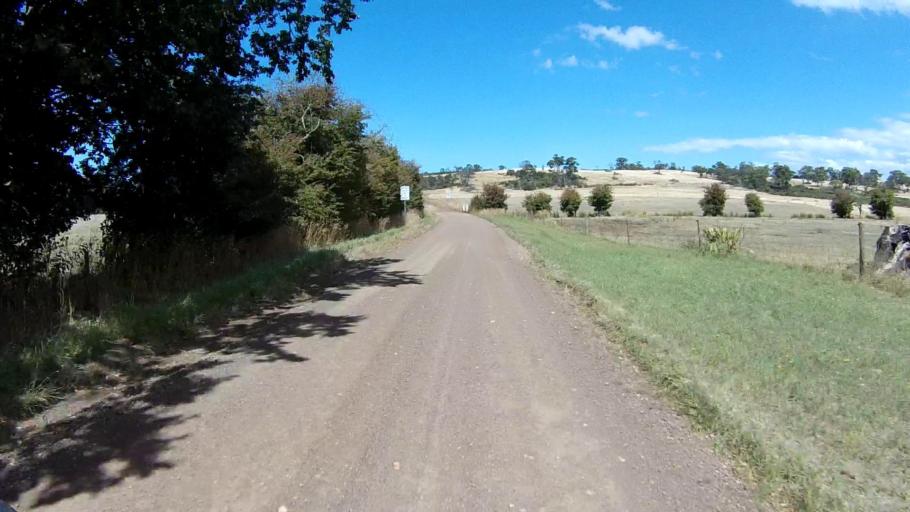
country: AU
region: Tasmania
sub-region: Break O'Day
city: St Helens
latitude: -41.9623
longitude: 148.0721
